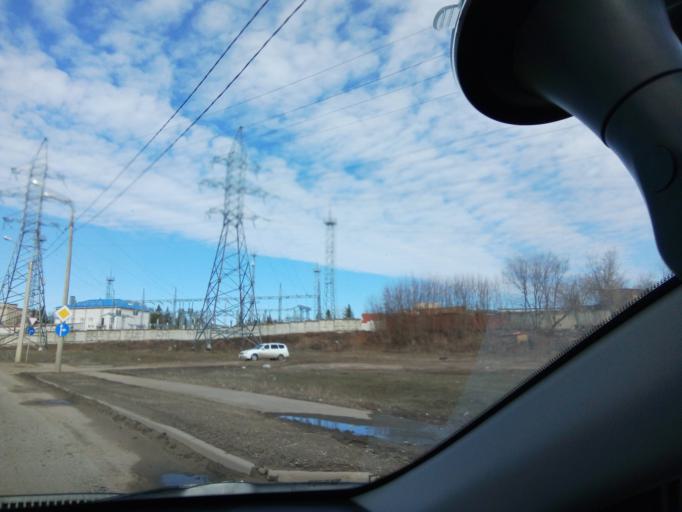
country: RU
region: Chuvashia
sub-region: Cheboksarskiy Rayon
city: Cheboksary
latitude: 56.1095
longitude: 47.2466
